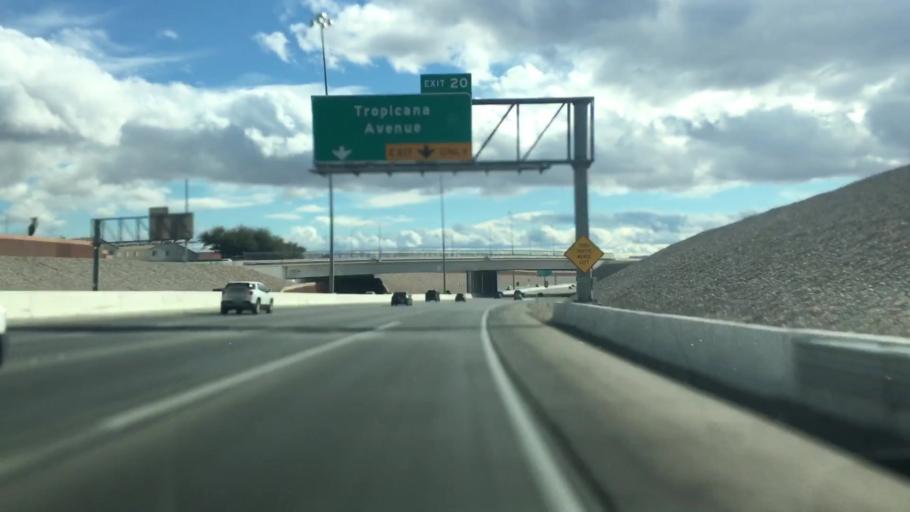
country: US
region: Nevada
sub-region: Clark County
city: Summerlin South
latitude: 36.1116
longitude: -115.2988
